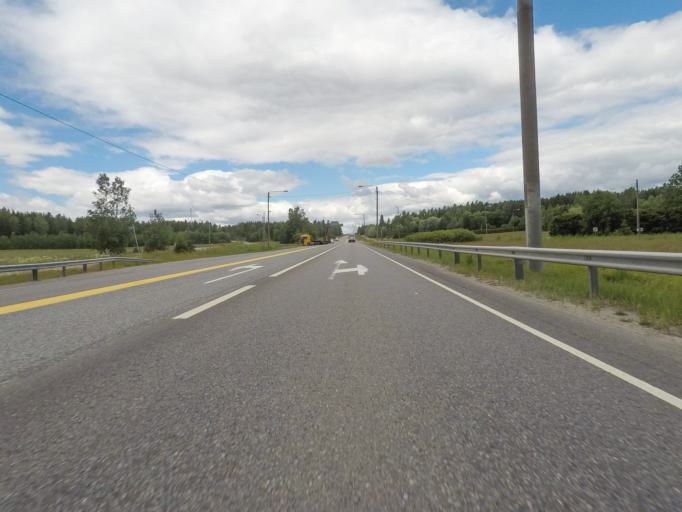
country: FI
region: Varsinais-Suomi
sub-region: Turku
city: Lieto
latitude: 60.4576
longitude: 22.4384
